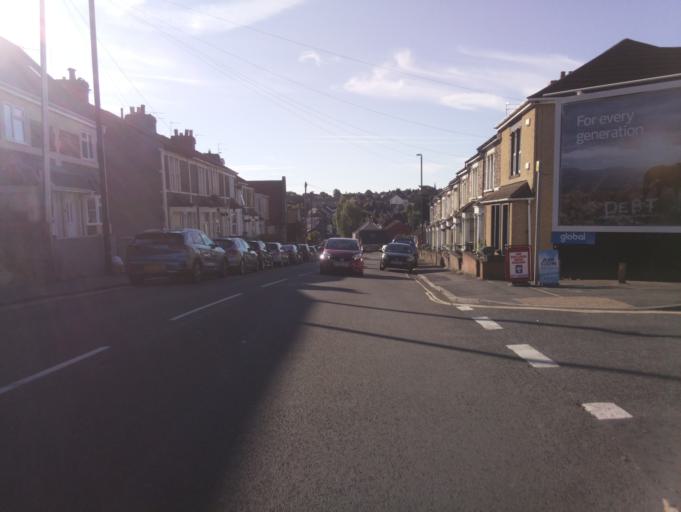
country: GB
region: England
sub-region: South Gloucestershire
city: Kingswood
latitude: 51.4584
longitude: -2.5325
